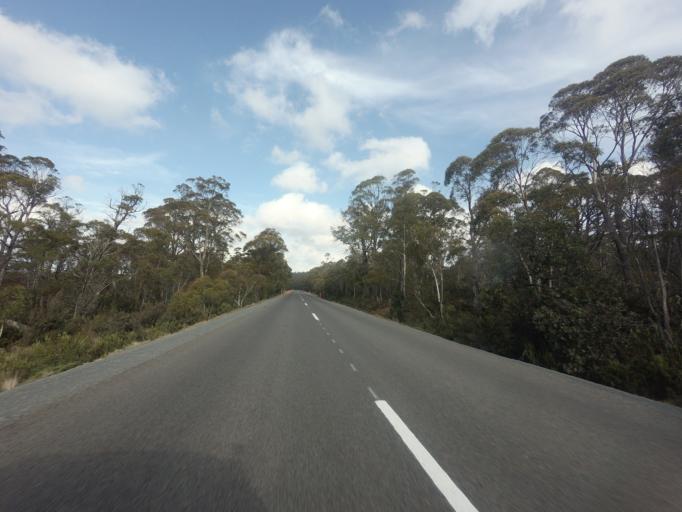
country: AU
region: Tasmania
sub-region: Meander Valley
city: Deloraine
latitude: -41.8355
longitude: 146.6795
